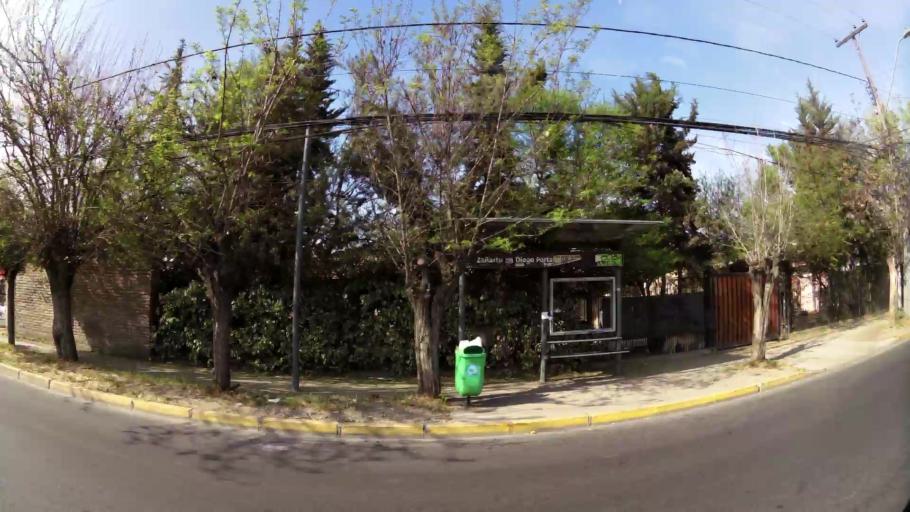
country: CL
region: Santiago Metropolitan
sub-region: Provincia de Cordillera
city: Puente Alto
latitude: -33.5628
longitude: -70.5792
